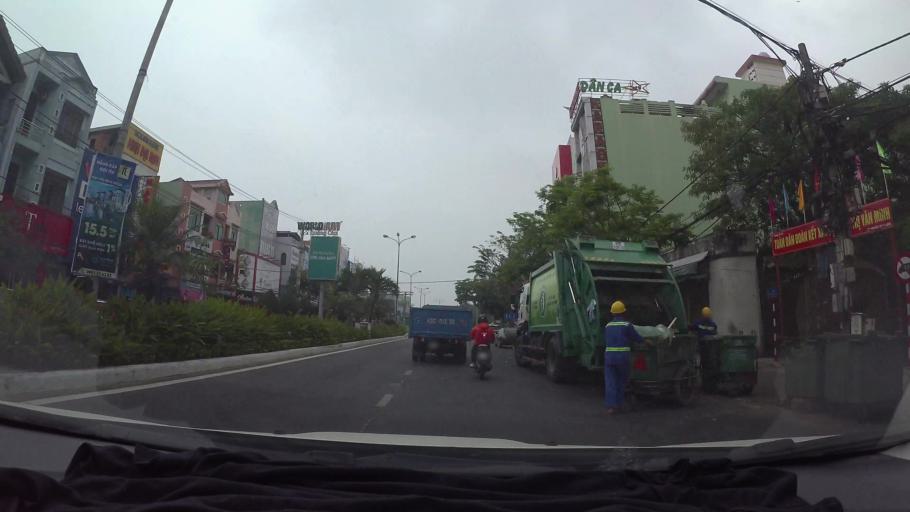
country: VN
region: Da Nang
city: Da Nang
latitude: 16.0575
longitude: 108.2066
